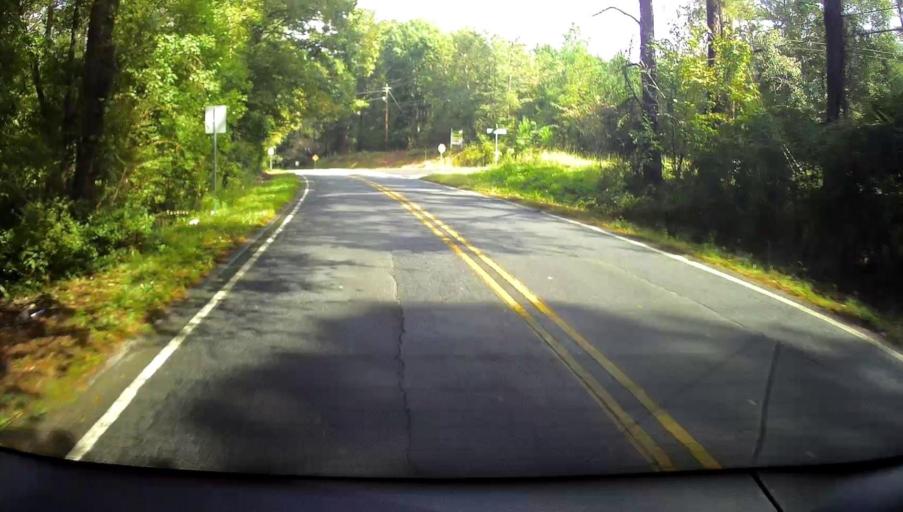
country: US
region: Georgia
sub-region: Bibb County
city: Macon
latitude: 32.9109
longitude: -83.7165
